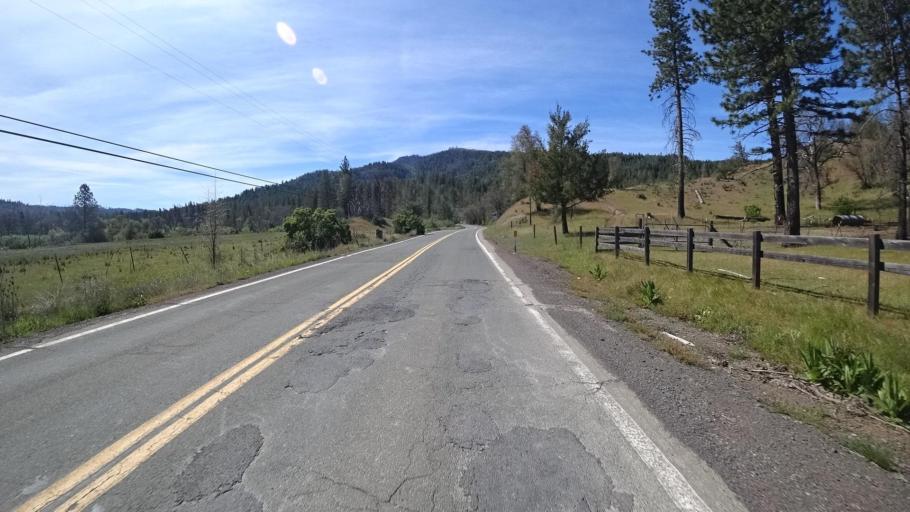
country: US
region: California
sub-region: Lake County
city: Cobb
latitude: 38.8391
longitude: -122.7469
